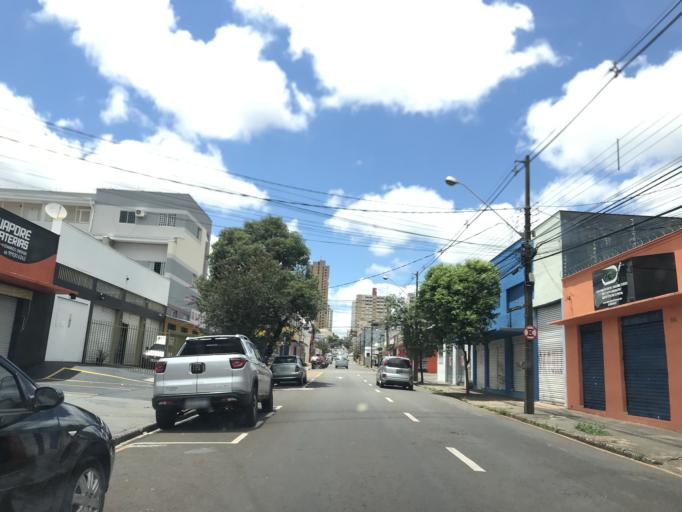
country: BR
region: Parana
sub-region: Londrina
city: Londrina
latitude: -23.3050
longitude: -51.1628
